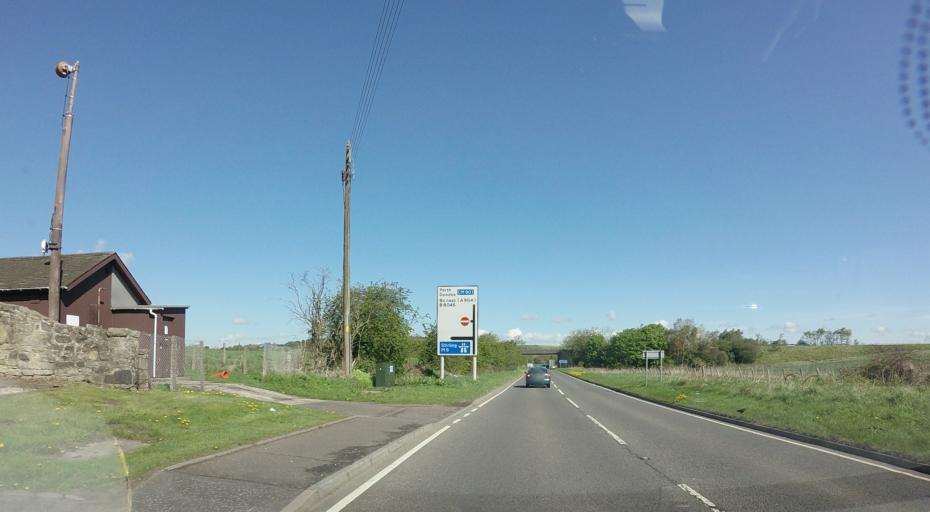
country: GB
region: Scotland
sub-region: West Lothian
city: Broxburn
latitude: 55.9797
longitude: -3.5090
